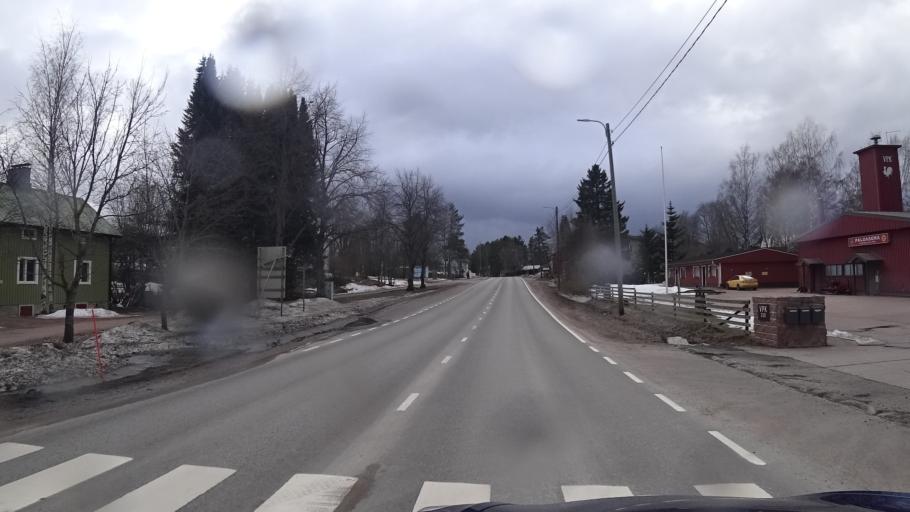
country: FI
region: Kymenlaakso
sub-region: Kotka-Hamina
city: Karhula
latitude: 60.5305
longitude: 26.9065
